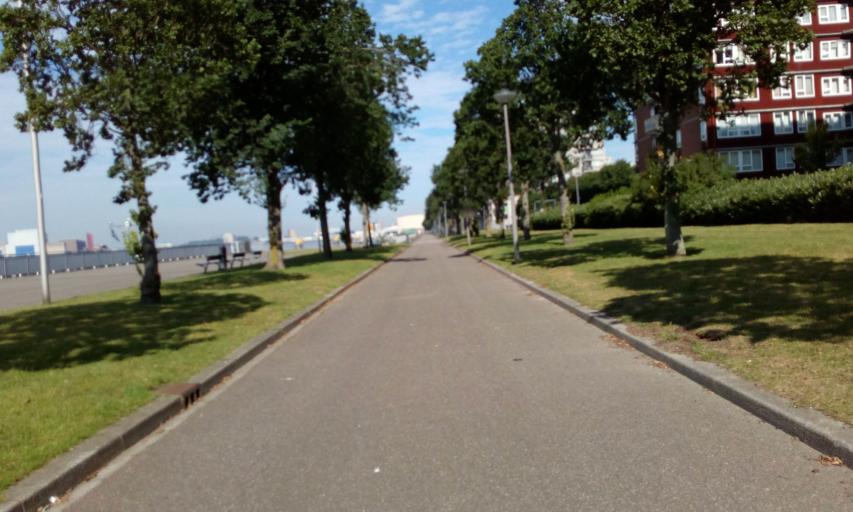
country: NL
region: South Holland
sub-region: Gemeente Rotterdam
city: Delfshaven
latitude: 51.9025
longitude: 4.4452
